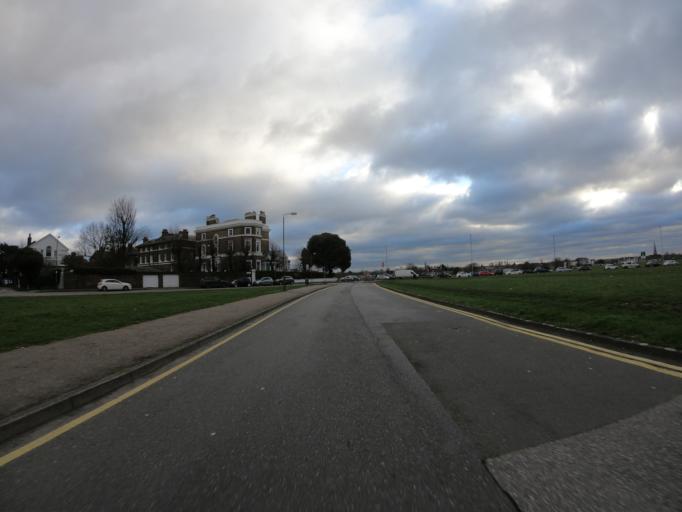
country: GB
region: England
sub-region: Greater London
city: Blackheath
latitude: 51.4738
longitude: 0.0117
